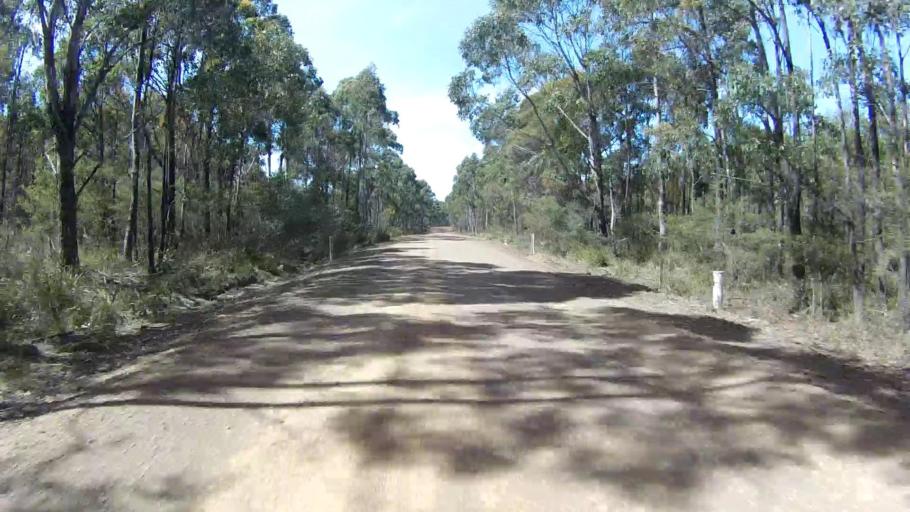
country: AU
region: Tasmania
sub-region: Sorell
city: Sorell
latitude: -42.6754
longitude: 147.7292
